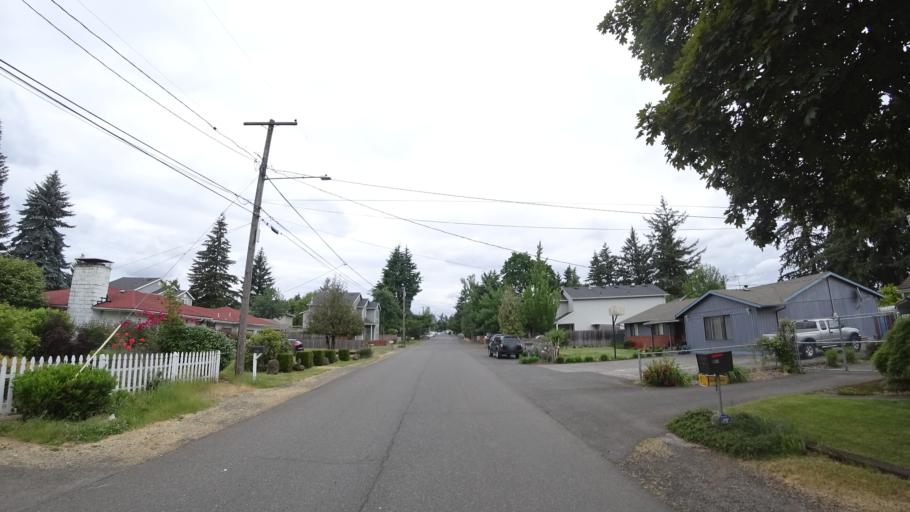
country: US
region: Oregon
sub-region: Multnomah County
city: Lents
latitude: 45.5011
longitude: -122.5409
